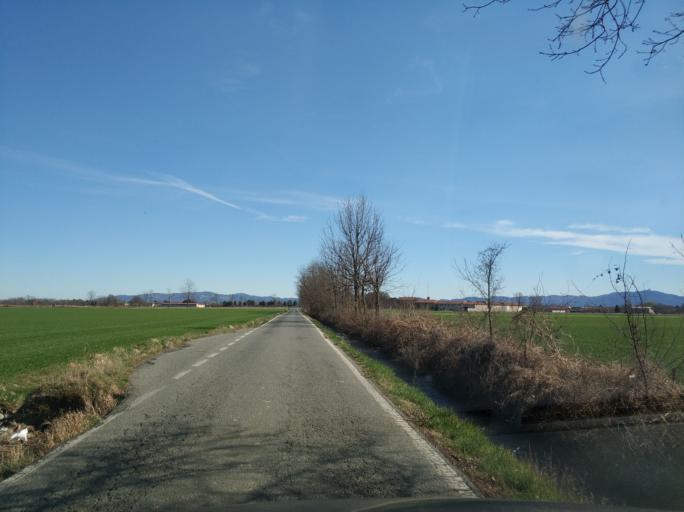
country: IT
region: Piedmont
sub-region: Provincia di Torino
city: Leini
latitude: 45.1963
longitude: 7.6809
